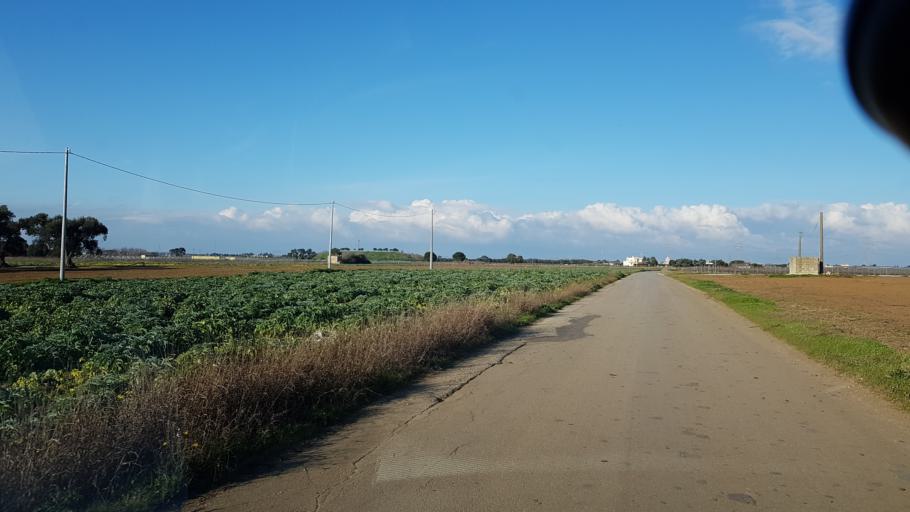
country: IT
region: Apulia
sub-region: Provincia di Brindisi
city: Tuturano
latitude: 40.5727
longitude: 17.8996
